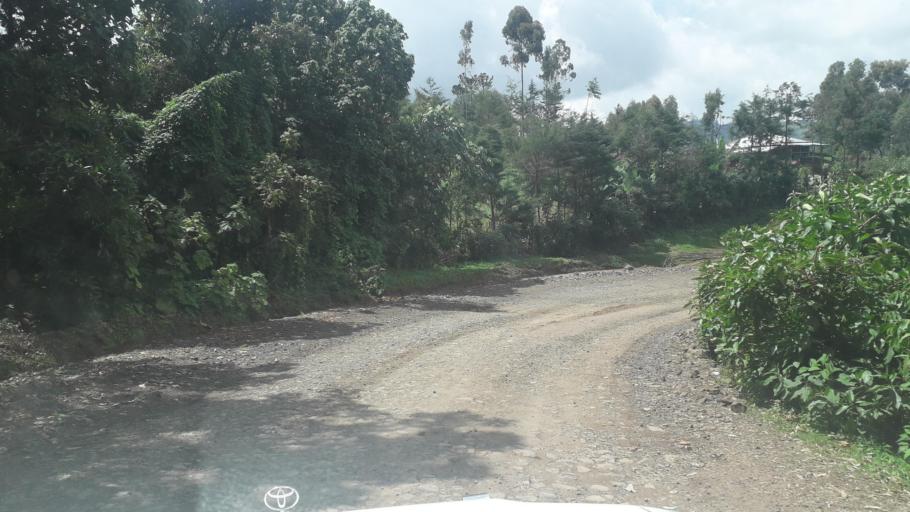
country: ET
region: Oromiya
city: Jima
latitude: 7.4538
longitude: 36.8715
